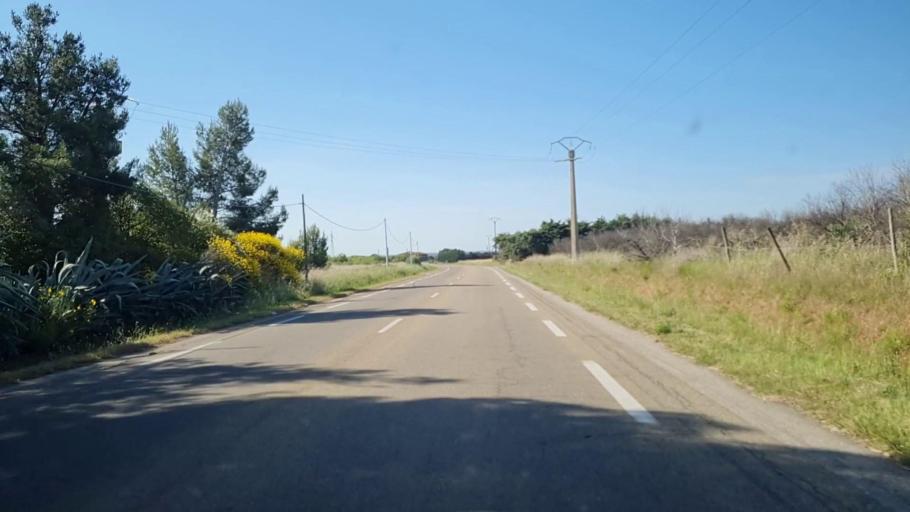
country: FR
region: Languedoc-Roussillon
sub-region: Departement du Gard
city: Saint-Gilles
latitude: 43.7035
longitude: 4.4229
